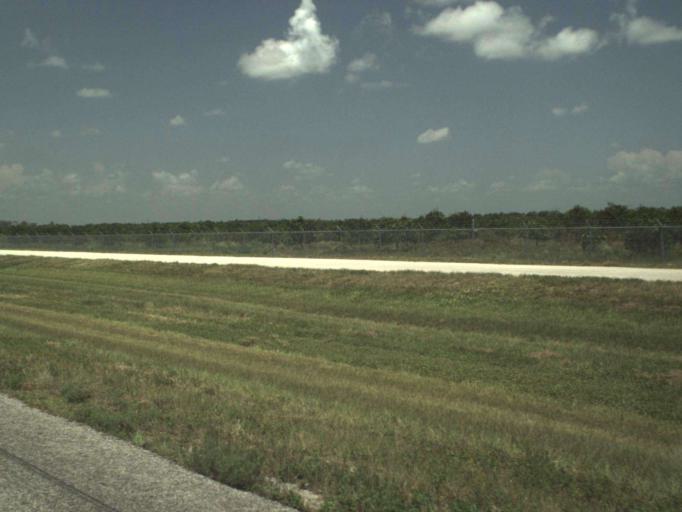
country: US
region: Florida
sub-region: Saint Lucie County
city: Fort Pierce South
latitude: 27.3690
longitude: -80.5096
